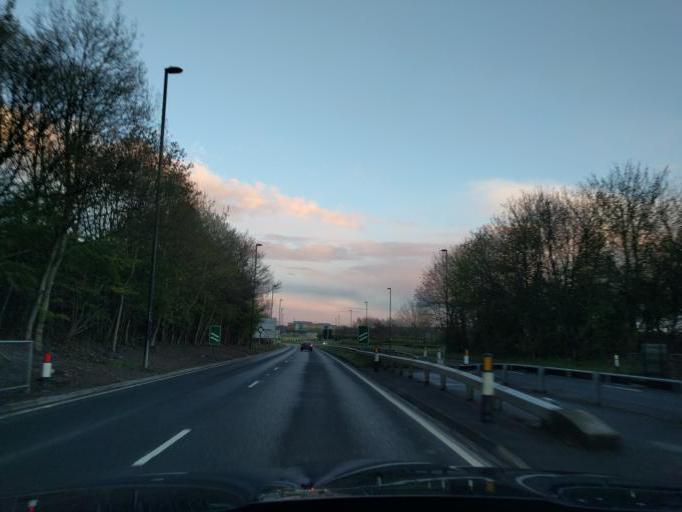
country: GB
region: England
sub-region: Newcastle upon Tyne
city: Gosforth
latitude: 55.0280
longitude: -1.5885
